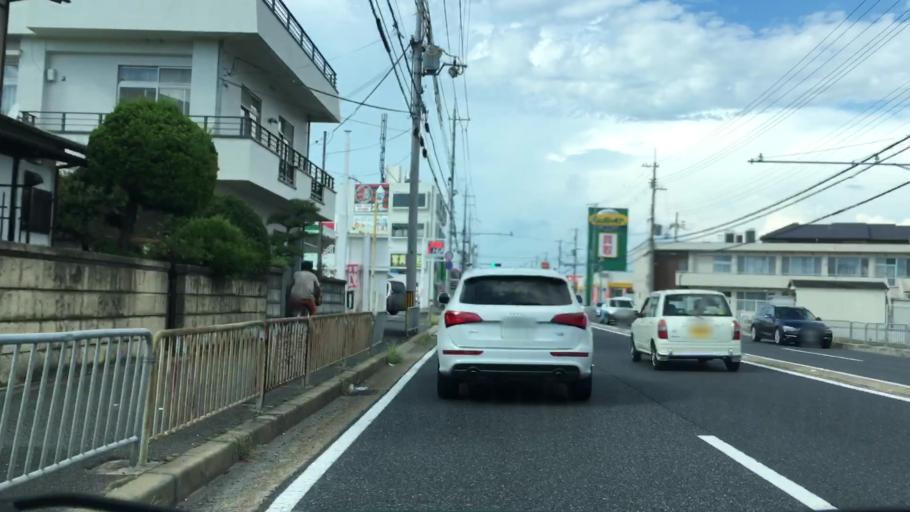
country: JP
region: Hyogo
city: Akashi
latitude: 34.6740
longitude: 134.9816
